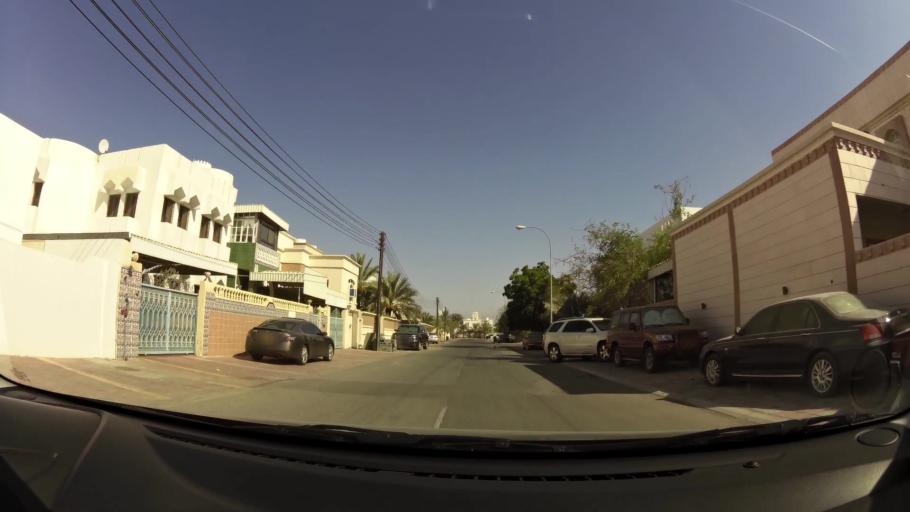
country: OM
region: Muhafazat Masqat
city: As Sib al Jadidah
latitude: 23.6306
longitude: 58.2062
